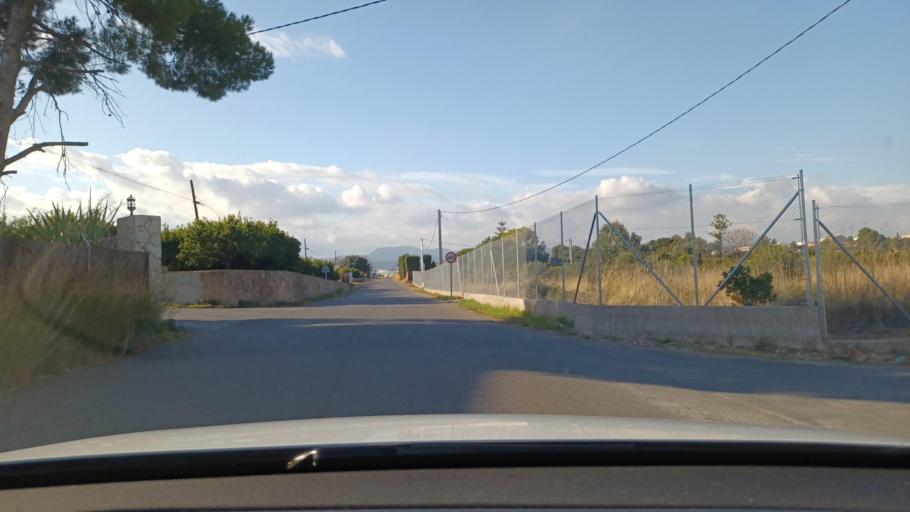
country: ES
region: Valencia
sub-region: Provincia de Castello
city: Onda
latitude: 39.9553
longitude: -0.2402
